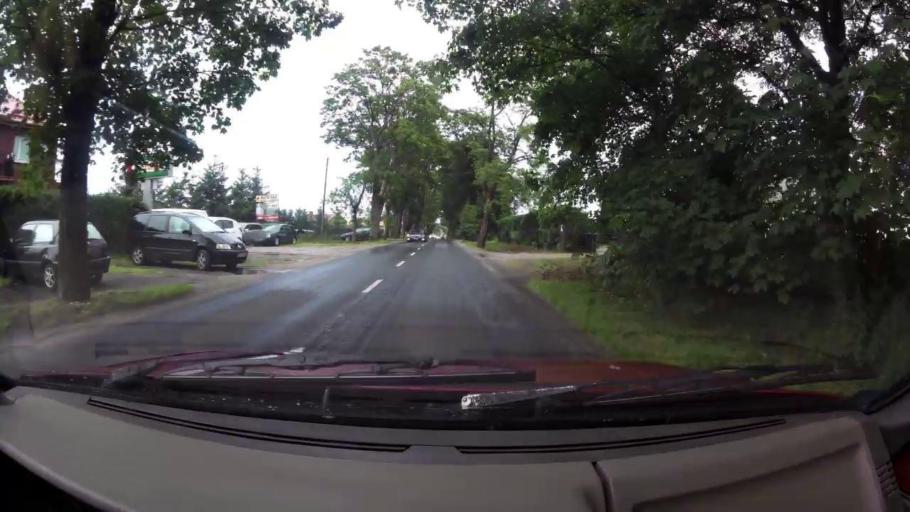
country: PL
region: West Pomeranian Voivodeship
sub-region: Koszalin
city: Koszalin
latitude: 54.1751
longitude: 16.1622
